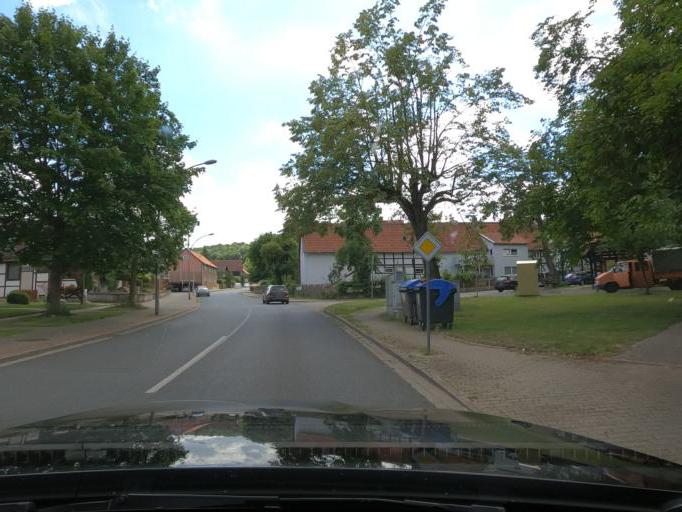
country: DE
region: Lower Saxony
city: Elbe
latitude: 52.1283
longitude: 10.2901
